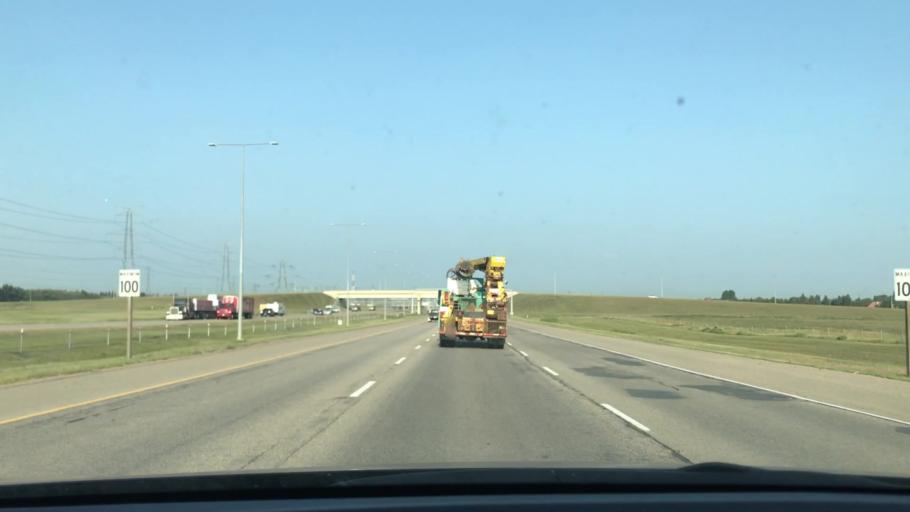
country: CA
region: Alberta
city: Beaumont
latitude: 53.4358
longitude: -113.4348
